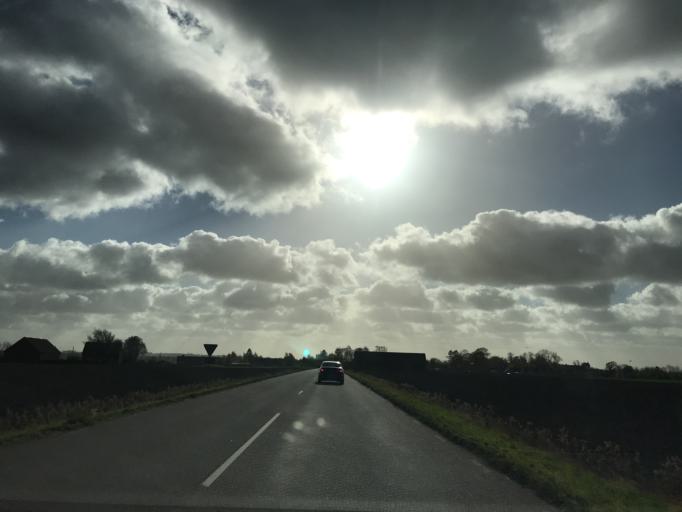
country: SE
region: Skane
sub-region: Helsingborg
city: Barslov
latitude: 56.0107
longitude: 12.8229
